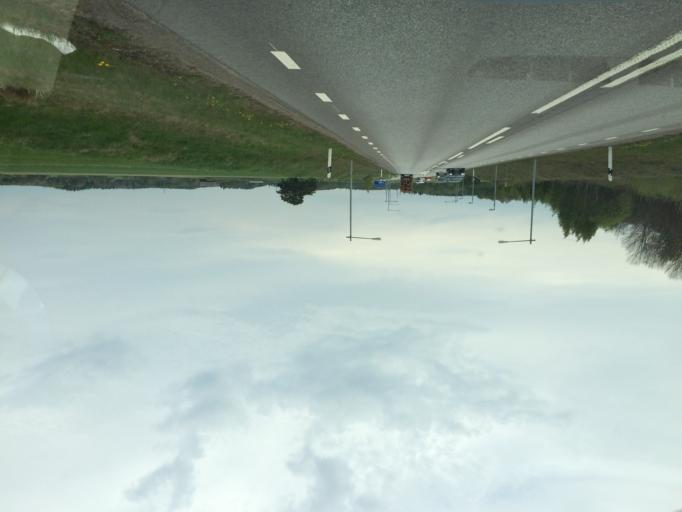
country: SE
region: Vaestmanland
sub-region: Kopings Kommun
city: Koping
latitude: 59.5256
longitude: 15.9627
